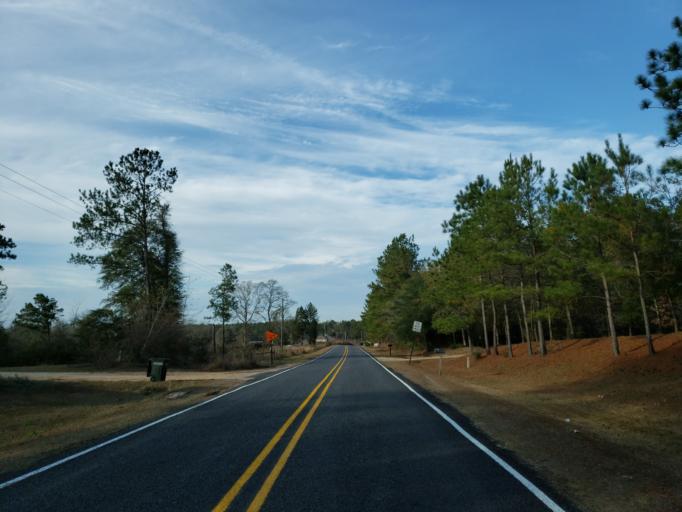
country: US
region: Mississippi
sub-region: Wayne County
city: Belmont
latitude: 31.4972
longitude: -88.5062
